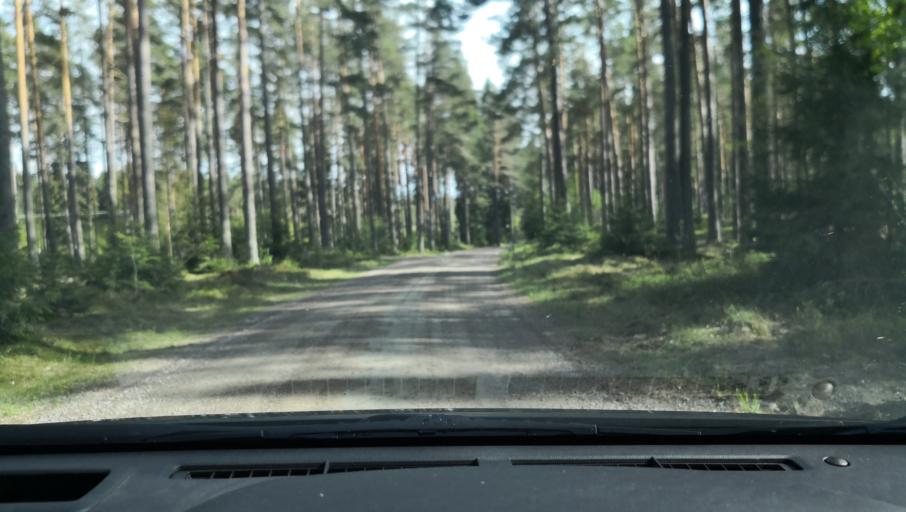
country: SE
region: OErebro
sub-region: Askersunds Kommun
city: Asbro
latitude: 59.0341
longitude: 15.0428
